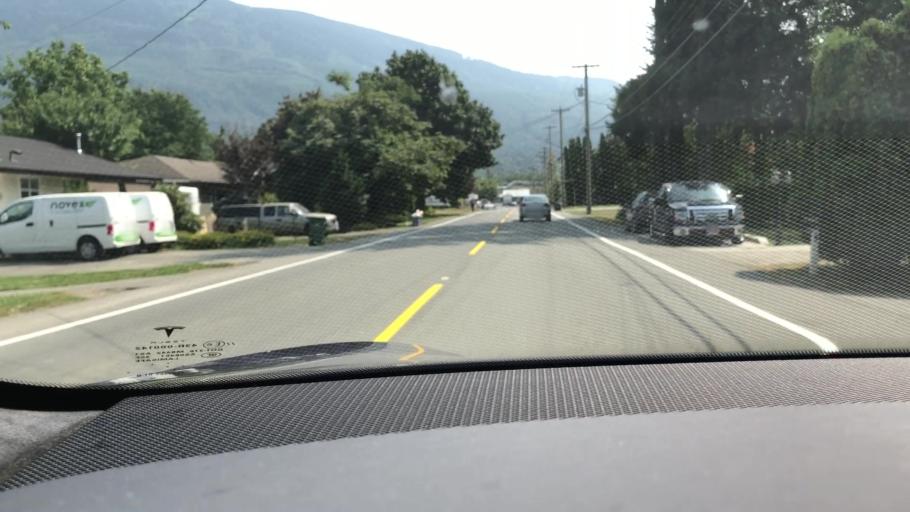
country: CA
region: British Columbia
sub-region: Fraser Valley Regional District
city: Chilliwack
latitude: 49.0842
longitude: -122.0649
